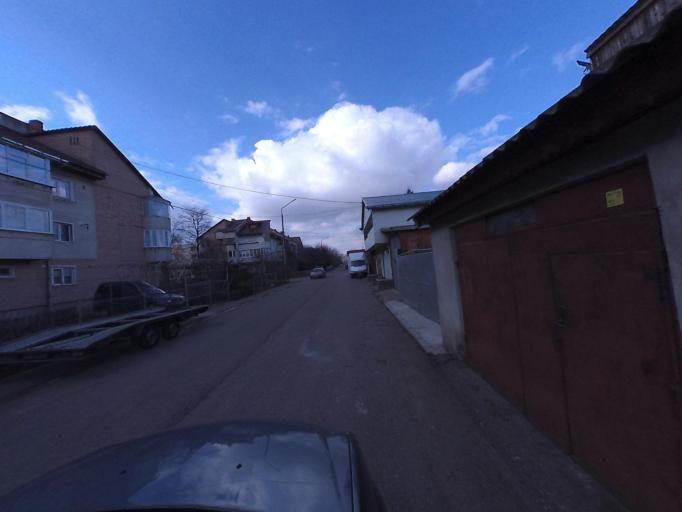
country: RO
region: Neamt
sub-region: Oras Targu Neamt
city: Targu Neamt
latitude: 47.2021
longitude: 26.3766
